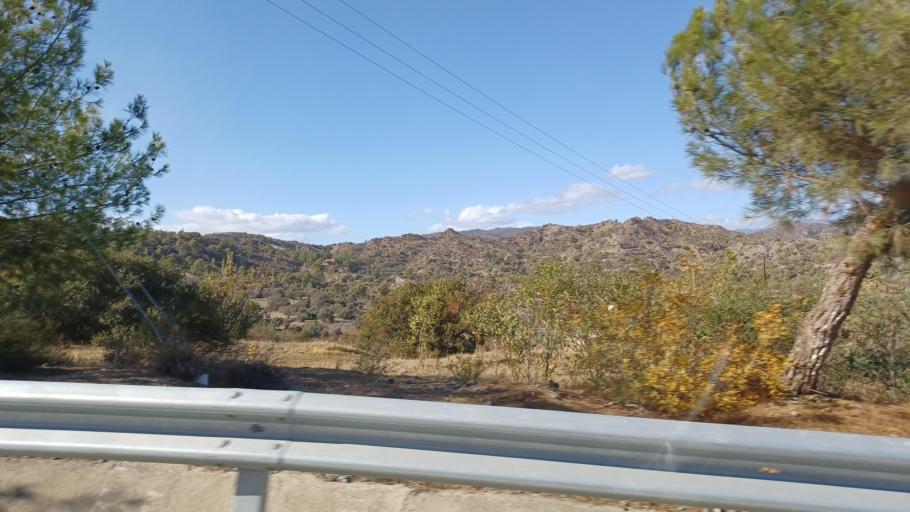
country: CY
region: Limassol
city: Pyrgos
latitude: 34.7749
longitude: 33.2474
